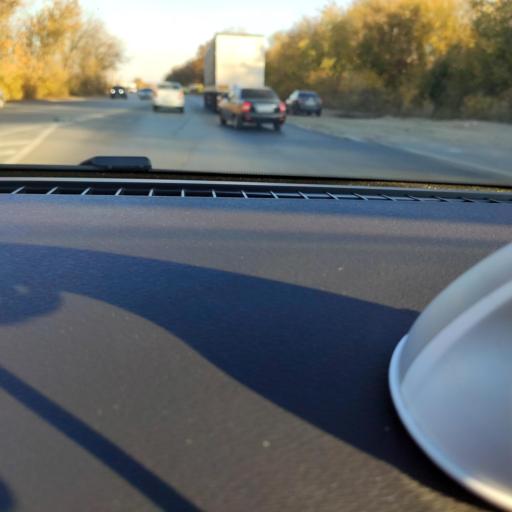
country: RU
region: Samara
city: Petra-Dubrava
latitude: 53.2741
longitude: 50.2659
